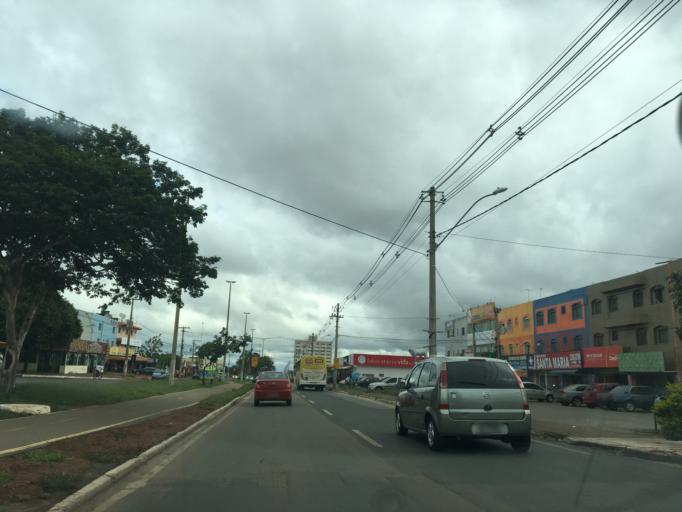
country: BR
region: Goias
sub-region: Luziania
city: Luziania
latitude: -16.0393
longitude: -48.0342
